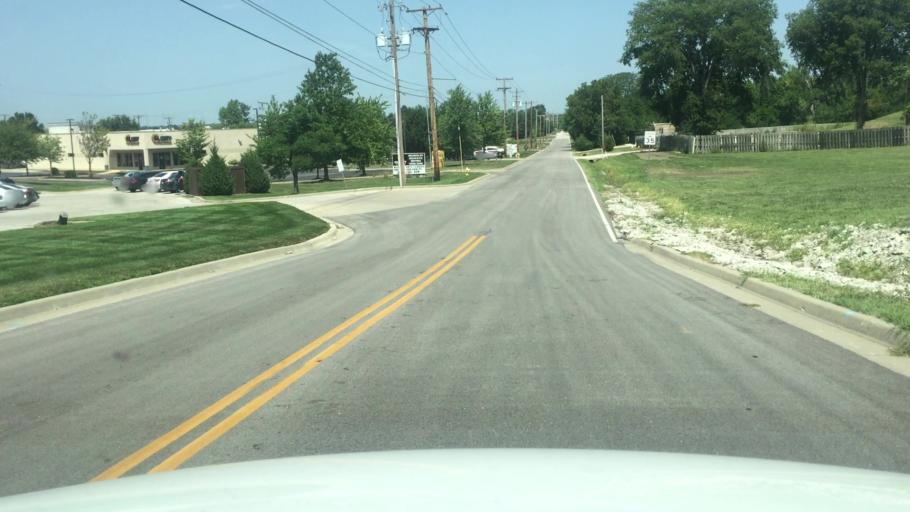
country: US
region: Missouri
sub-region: Jackson County
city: Lees Summit
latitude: 38.9255
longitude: -94.3818
